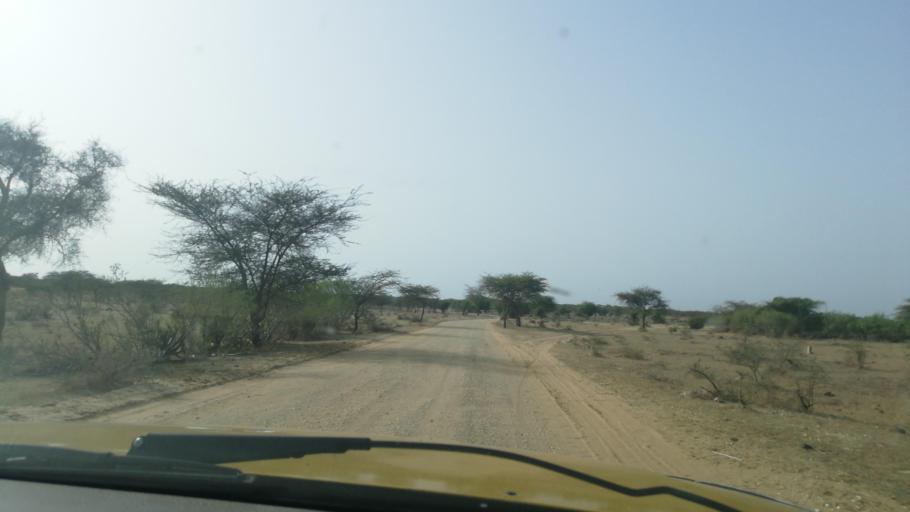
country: SN
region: Saint-Louis
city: Saint-Louis
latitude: 16.0578
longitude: -16.3325
